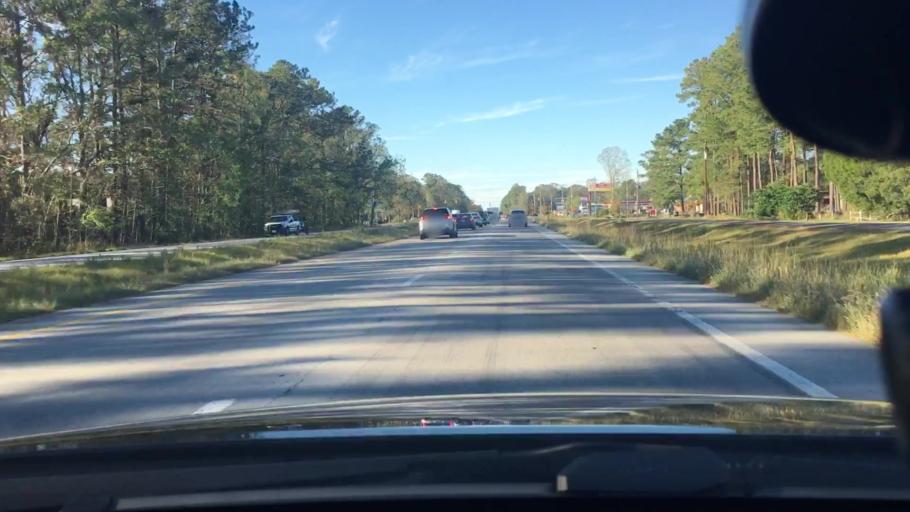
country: US
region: North Carolina
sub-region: Craven County
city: Fairfield Harbour
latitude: 35.0352
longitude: -77.0056
